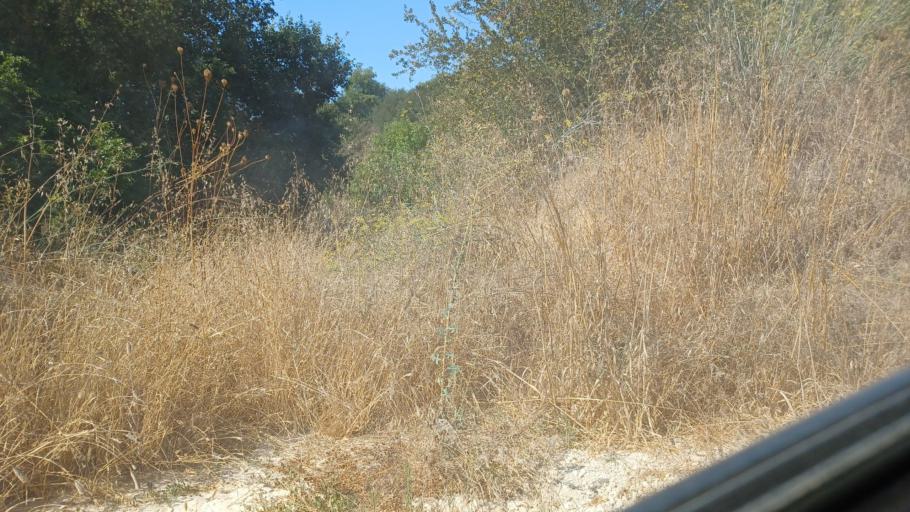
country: CY
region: Pafos
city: Mesogi
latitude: 34.8837
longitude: 32.5325
